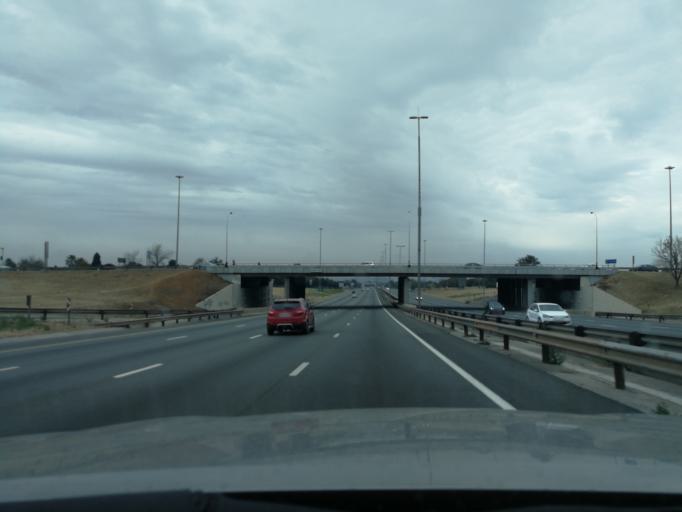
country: ZA
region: Gauteng
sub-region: Ekurhuleni Metropolitan Municipality
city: Germiston
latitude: -26.2645
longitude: 28.1506
